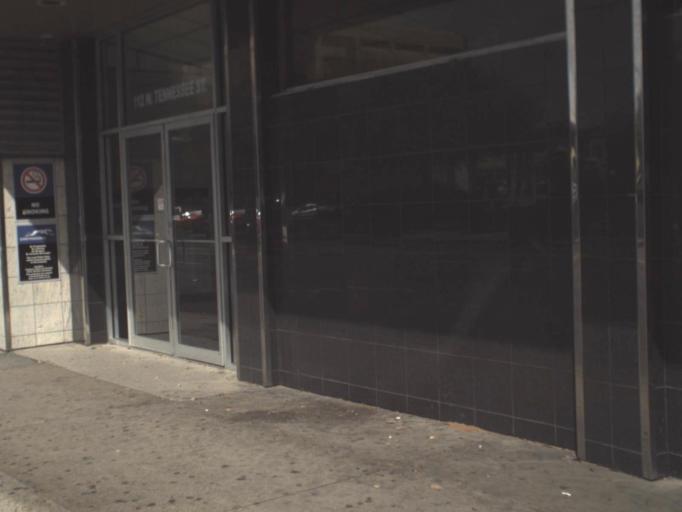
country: US
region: Florida
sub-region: Leon County
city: Tallahassee
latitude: 30.4448
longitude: -84.2824
